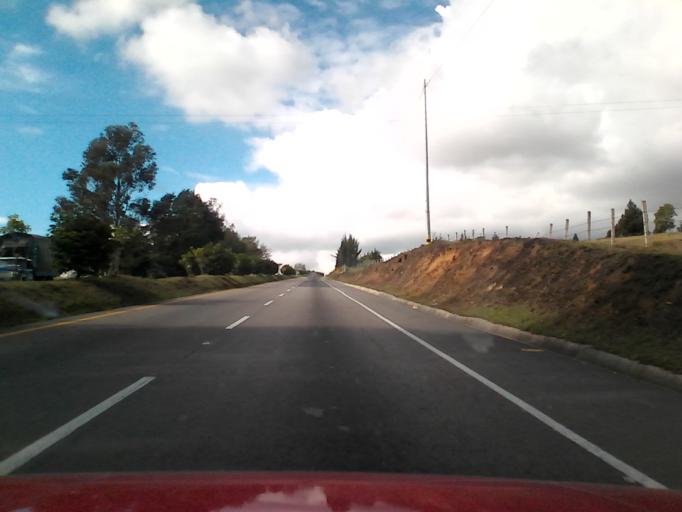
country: CO
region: Boyaca
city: Combita
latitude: 5.6323
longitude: -73.2972
